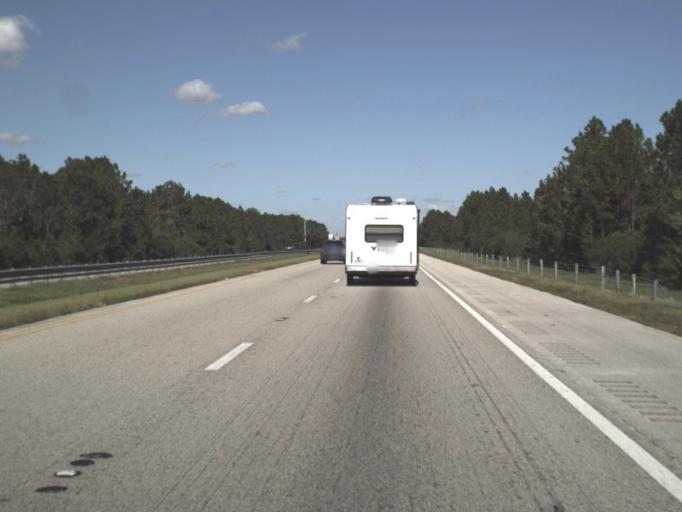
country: US
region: Florida
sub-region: Osceola County
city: Saint Cloud
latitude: 27.9139
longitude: -81.0534
